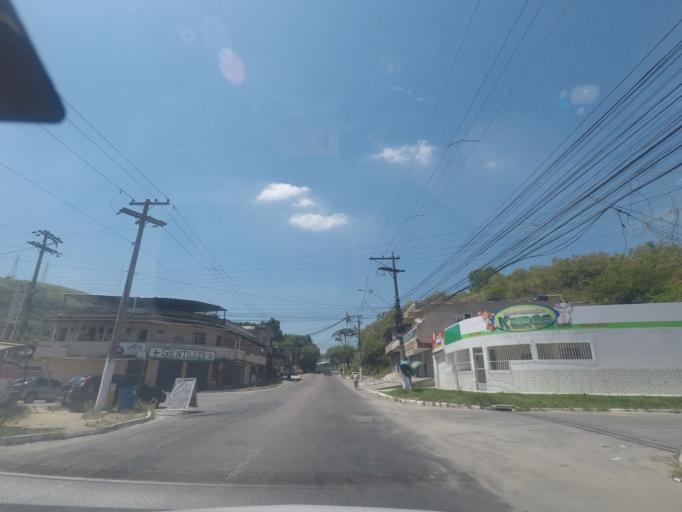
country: BR
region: Rio de Janeiro
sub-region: Petropolis
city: Petropolis
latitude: -22.5987
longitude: -43.1874
